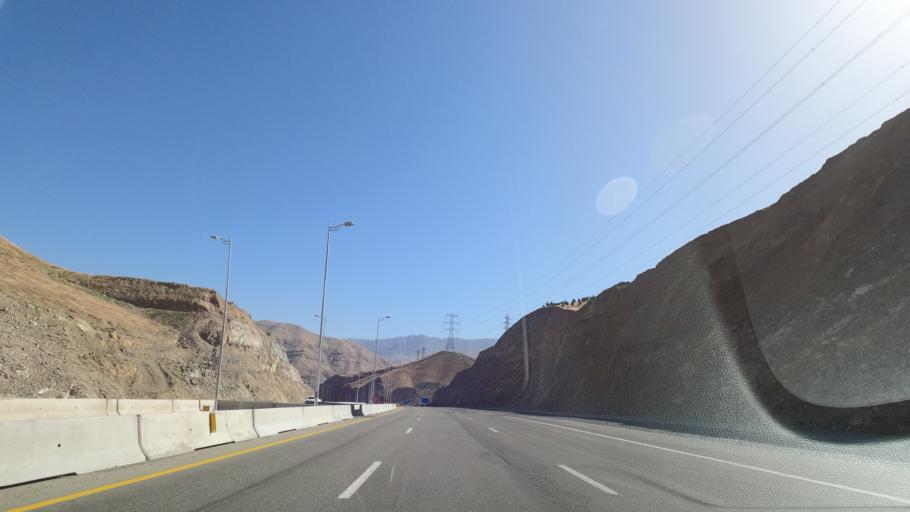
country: IR
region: Alborz
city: Karaj
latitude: 35.8130
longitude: 51.0367
